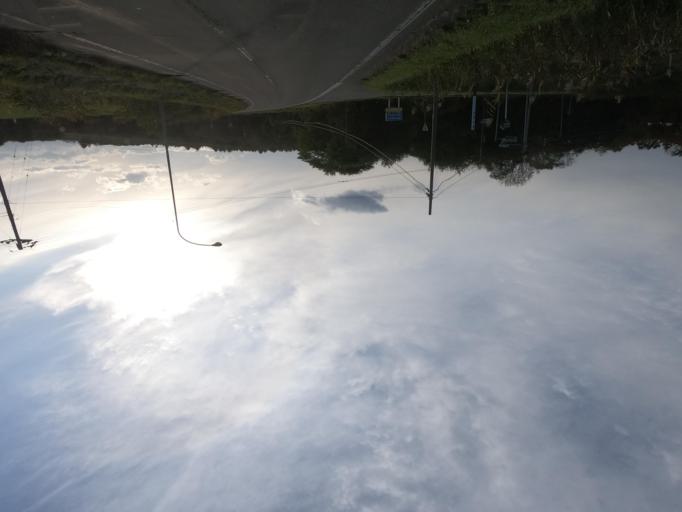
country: JP
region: Hokkaido
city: Obihiro
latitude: 42.5029
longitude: 143.4166
